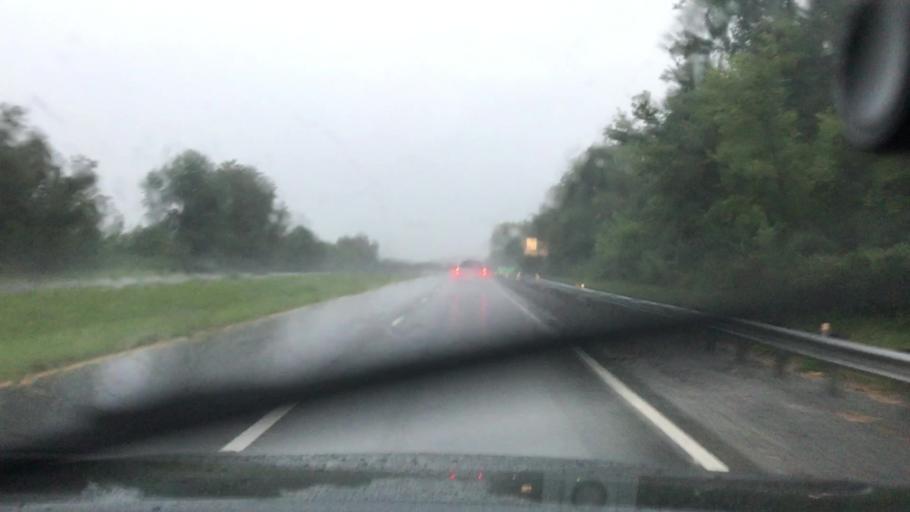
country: US
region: Virginia
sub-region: Giles County
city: Pearisburg
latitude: 37.3376
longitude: -80.7303
